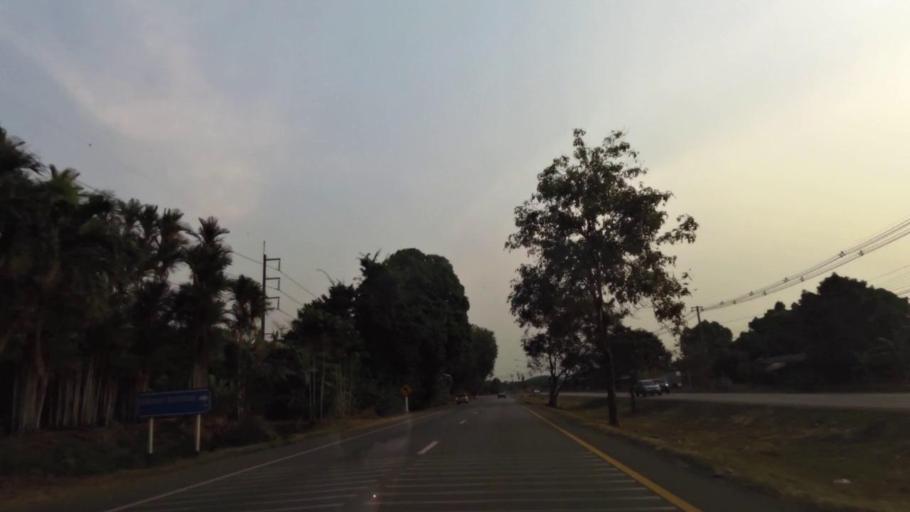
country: TH
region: Chanthaburi
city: Khlung
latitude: 12.4901
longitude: 102.1742
